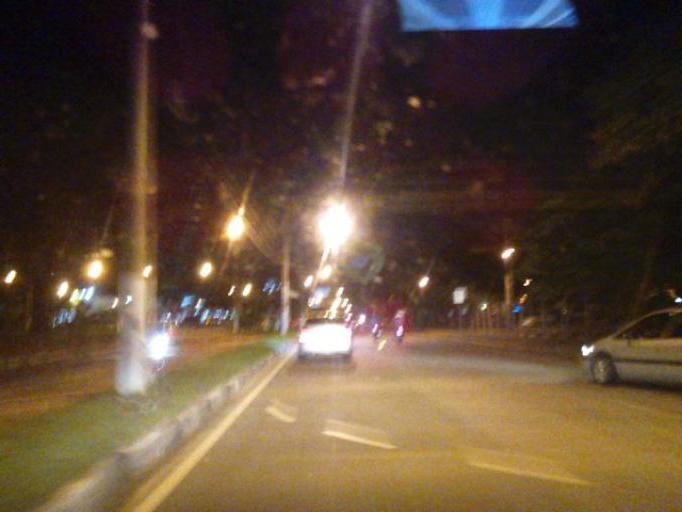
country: BR
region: Sao Paulo
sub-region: Jacarei
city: Jacarei
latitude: -23.2876
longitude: -45.9536
